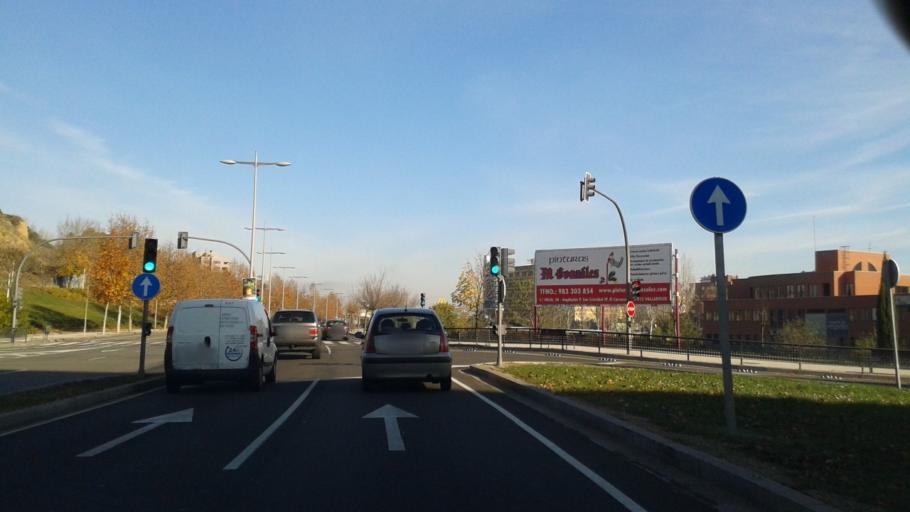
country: ES
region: Castille and Leon
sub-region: Provincia de Valladolid
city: Valladolid
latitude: 41.6338
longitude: -4.7497
